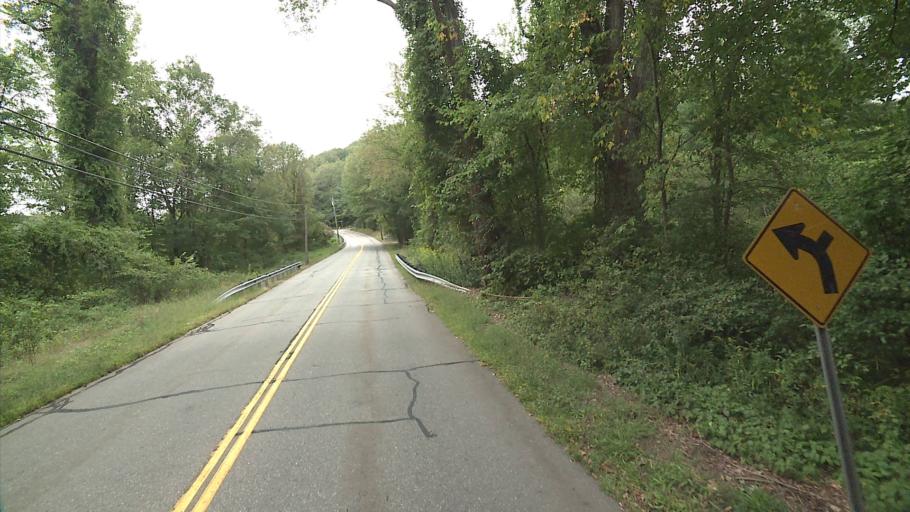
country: US
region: Connecticut
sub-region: Tolland County
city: South Coventry
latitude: 41.7828
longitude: -72.2826
